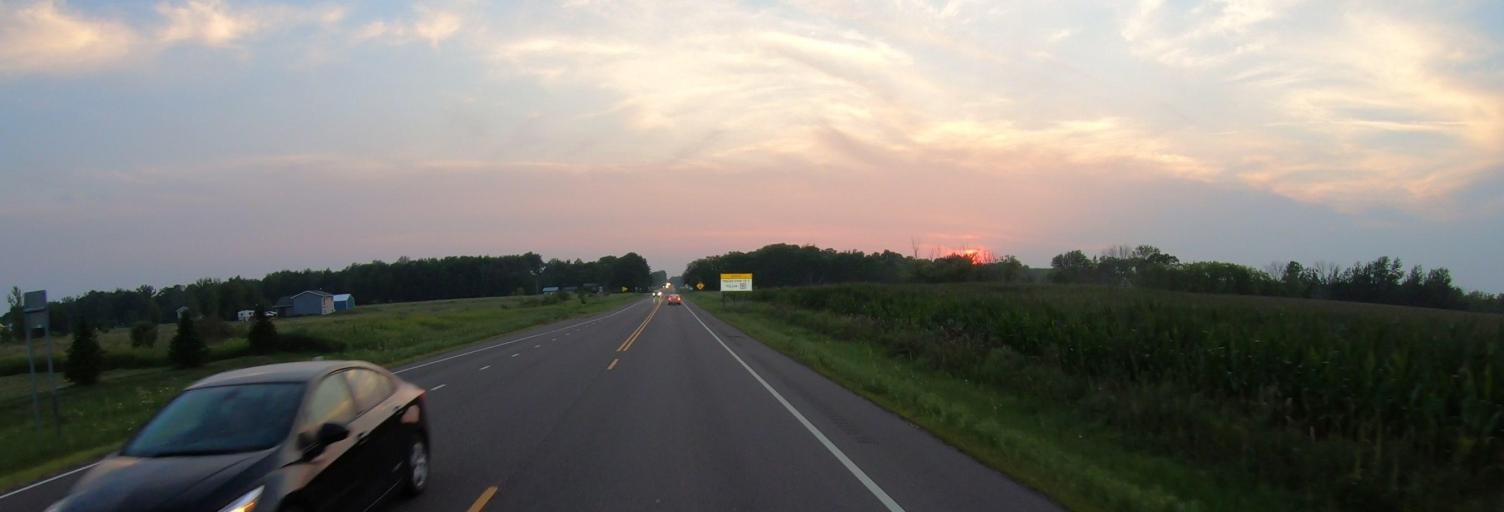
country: US
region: Minnesota
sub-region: Pine County
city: Rock Creek
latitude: 45.7737
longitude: -92.9558
